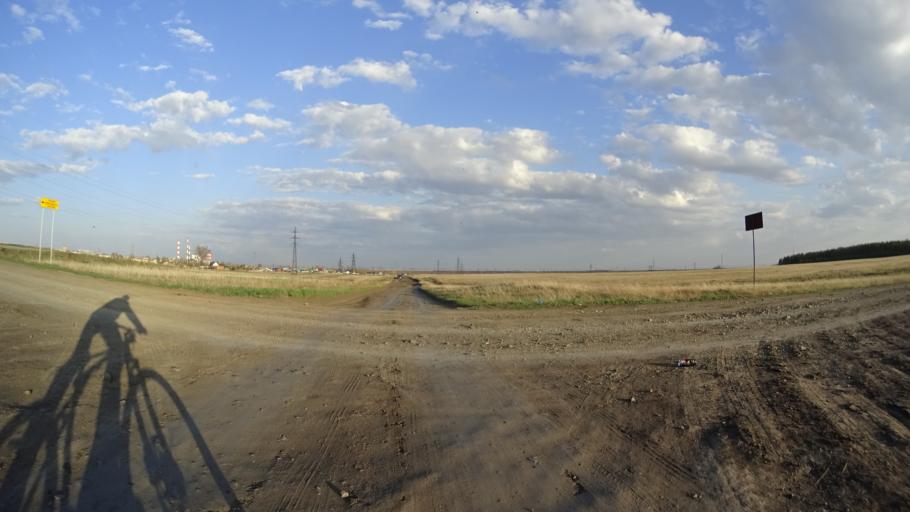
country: RU
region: Chelyabinsk
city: Troitsk
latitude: 54.0499
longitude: 61.5950
